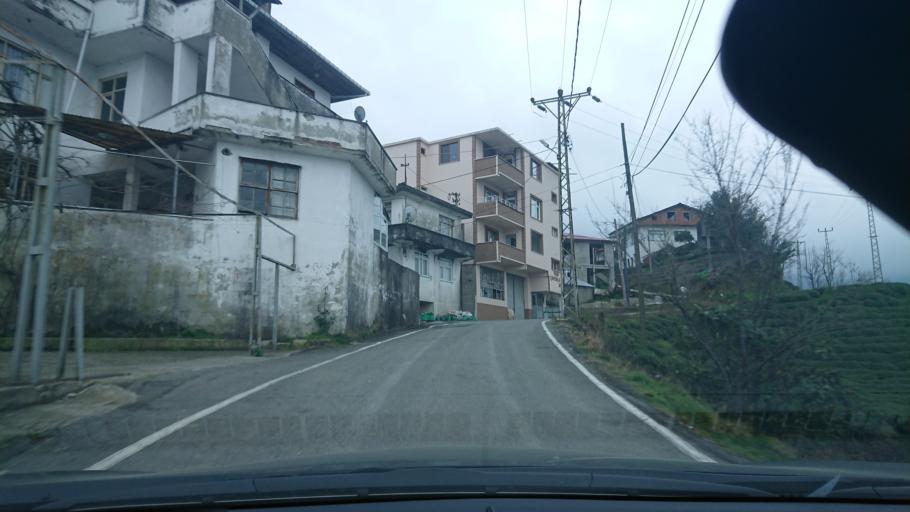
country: TR
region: Rize
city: Rize
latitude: 40.9975
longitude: 40.4895
